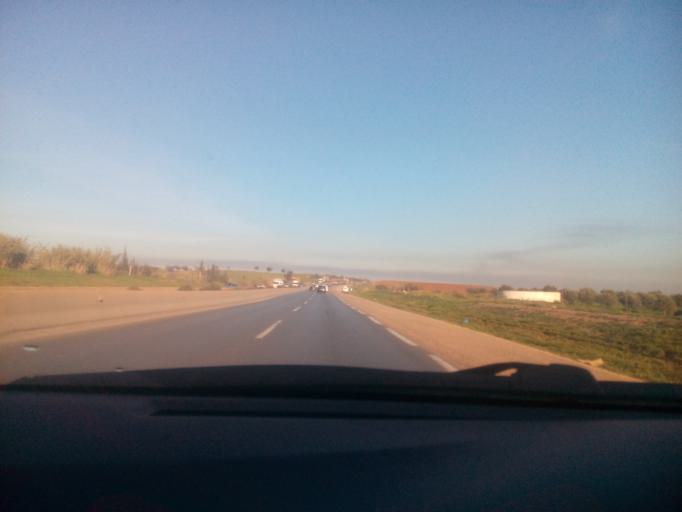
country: DZ
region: Oran
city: Bir el Djir
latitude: 35.7655
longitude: -0.4623
